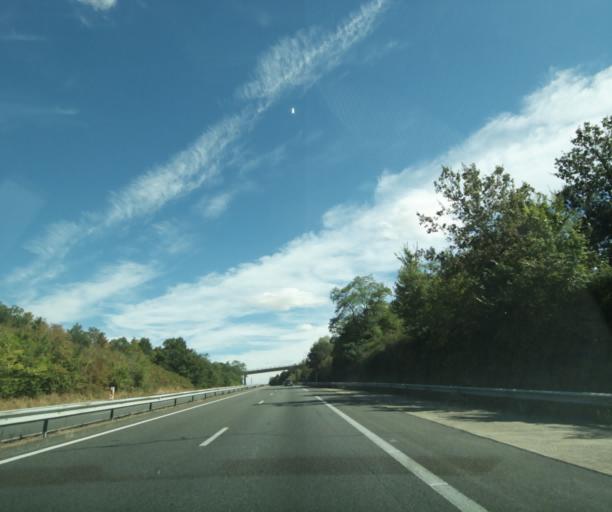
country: FR
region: Midi-Pyrenees
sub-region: Departement du Tarn-et-Garonne
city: Lamagistere
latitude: 44.0703
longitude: 0.8180
